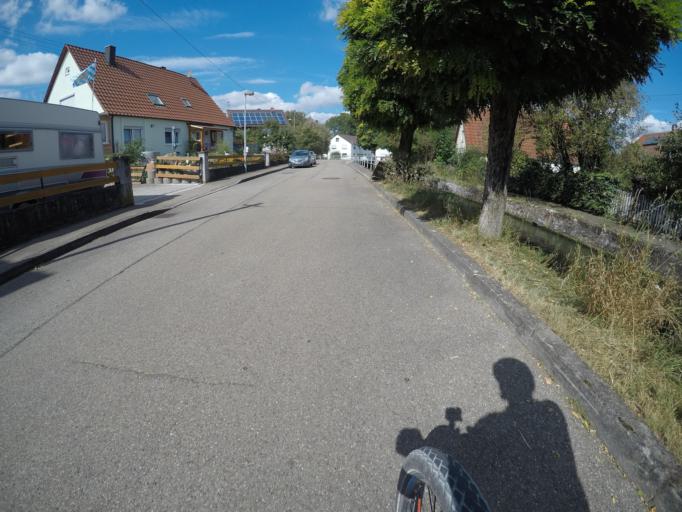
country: DE
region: Bavaria
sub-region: Swabia
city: Wittislingen
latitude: 48.6193
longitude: 10.4120
